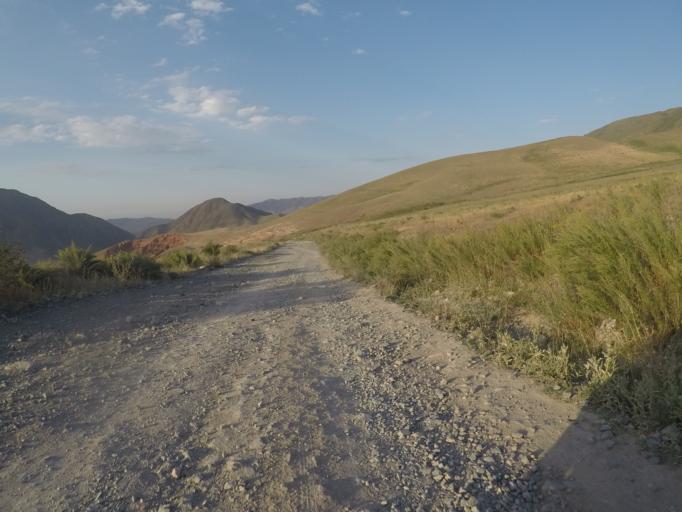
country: KG
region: Chuy
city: Bishkek
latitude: 42.6570
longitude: 74.6524
